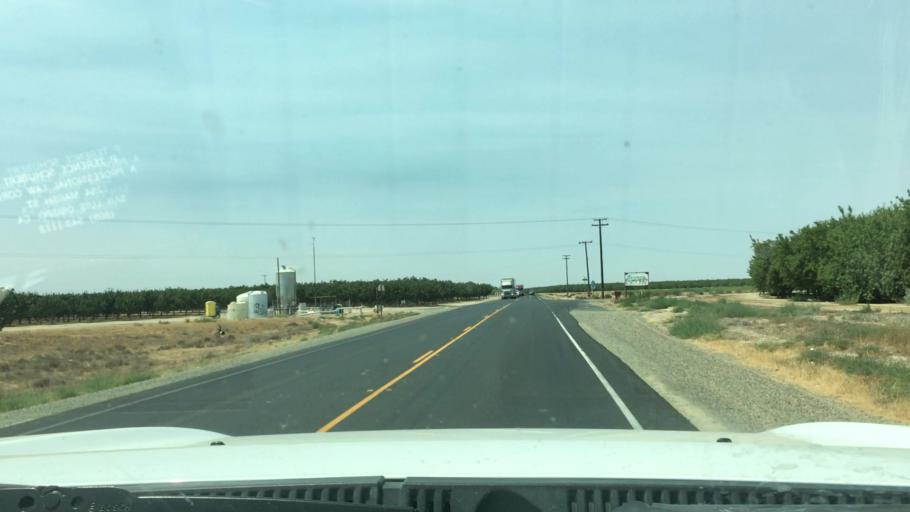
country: US
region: California
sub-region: Kern County
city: Lost Hills
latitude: 35.6067
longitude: -119.5796
